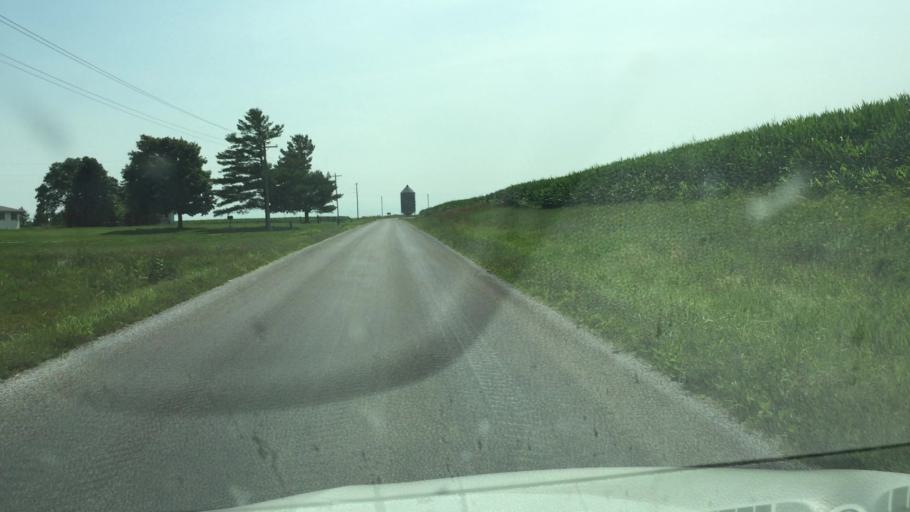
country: US
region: Illinois
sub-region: Hancock County
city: Nauvoo
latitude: 40.5112
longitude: -91.3311
